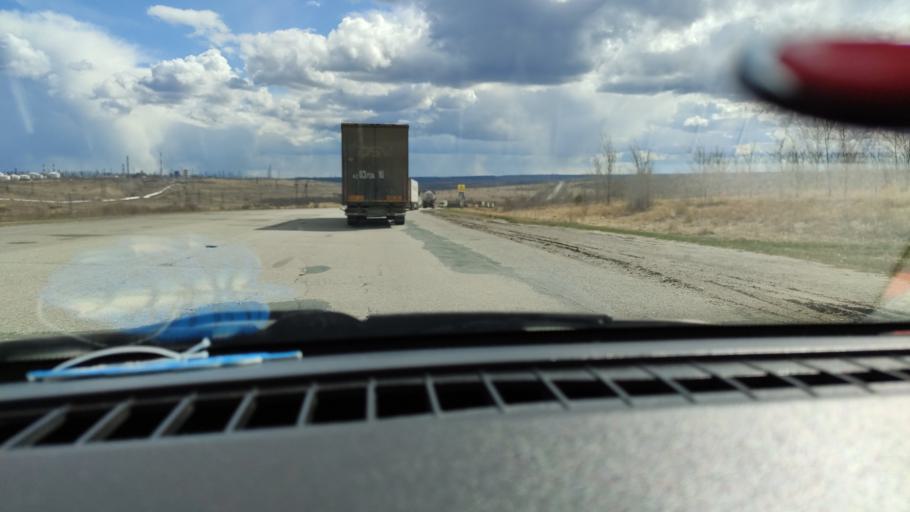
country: RU
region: Samara
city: Varlamovo
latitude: 53.1041
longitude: 48.3571
